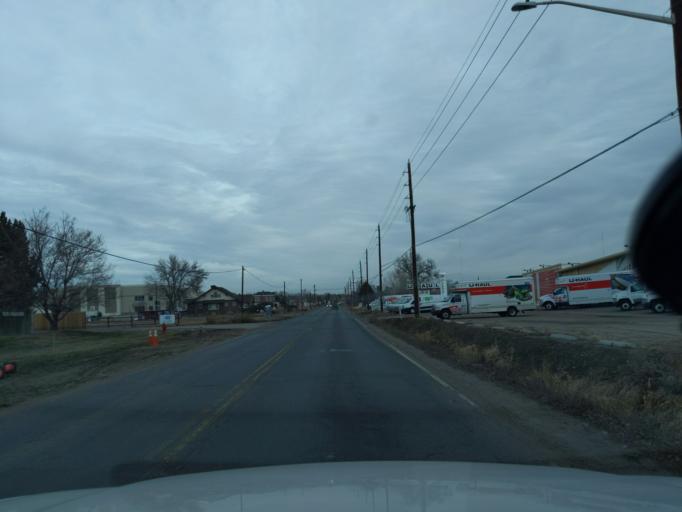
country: US
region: Colorado
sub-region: Adams County
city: Welby
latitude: 39.8330
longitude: -104.9591
